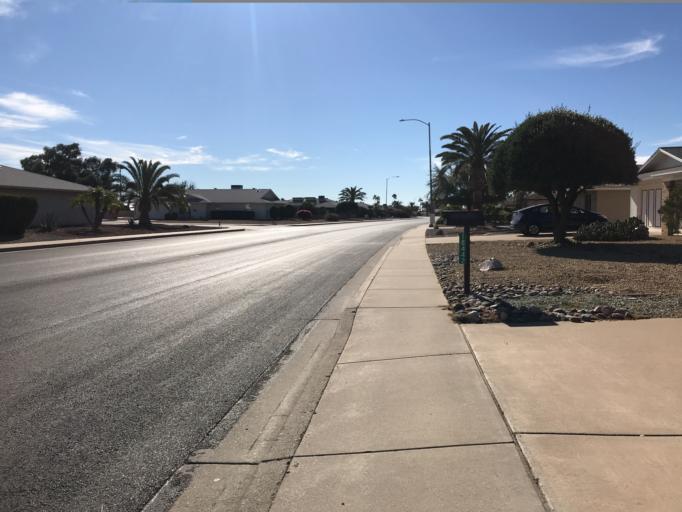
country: US
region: Arizona
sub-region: Maricopa County
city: Sun City West
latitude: 33.6532
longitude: -112.3261
